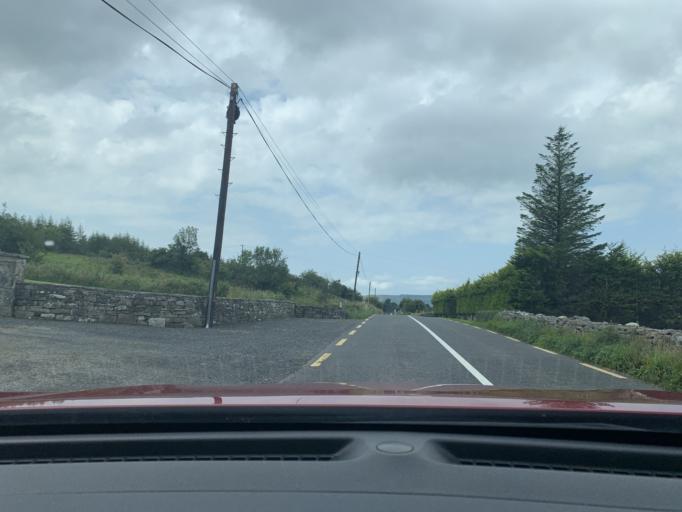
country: IE
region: Connaught
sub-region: Maigh Eo
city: Kiltamagh
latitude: 53.8506
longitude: -8.9721
